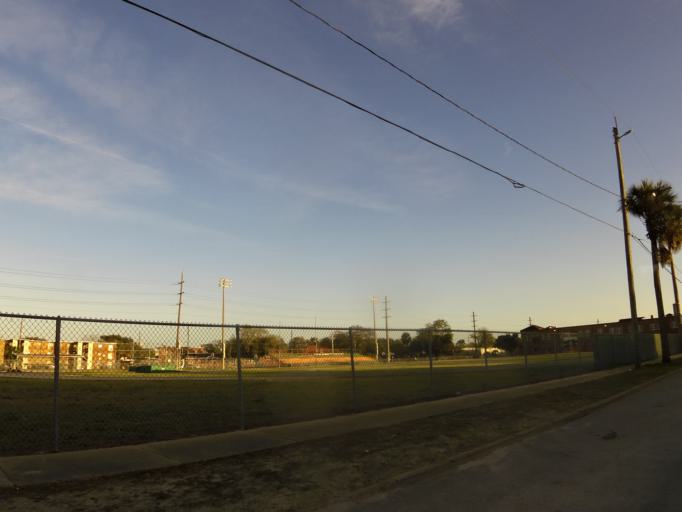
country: US
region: Florida
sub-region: Duval County
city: Jacksonville
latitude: 30.3435
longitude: -81.6404
